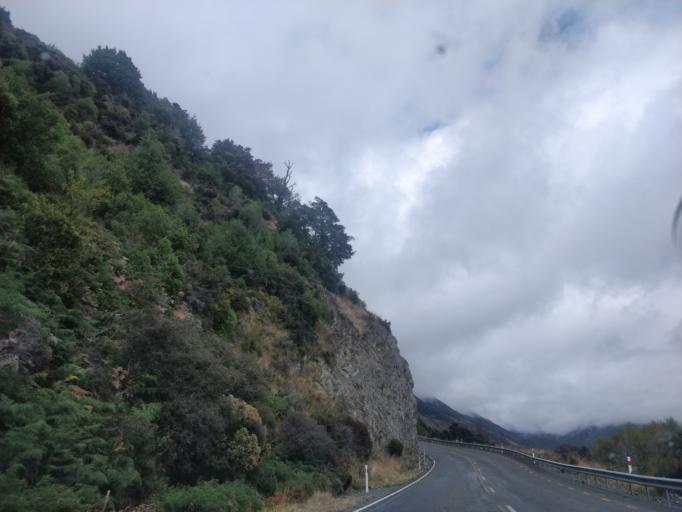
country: NZ
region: Canterbury
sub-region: Waimakariri District
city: Oxford
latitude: -43.0157
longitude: 171.7087
